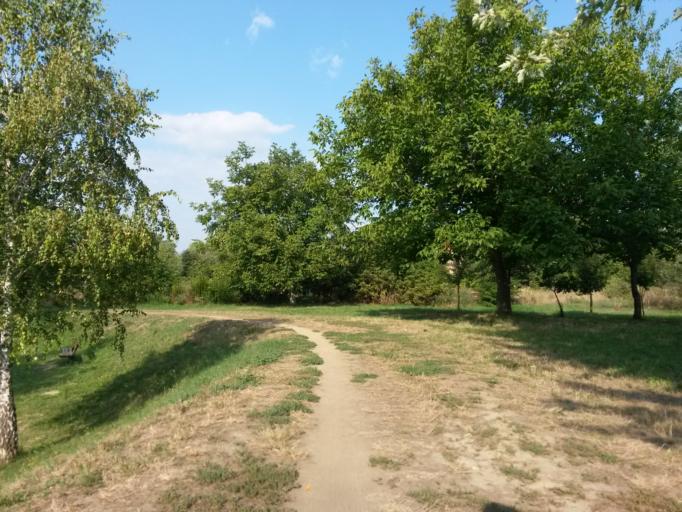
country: HR
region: Osjecko-Baranjska
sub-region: Grad Osijek
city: Osijek
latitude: 45.5427
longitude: 18.7233
